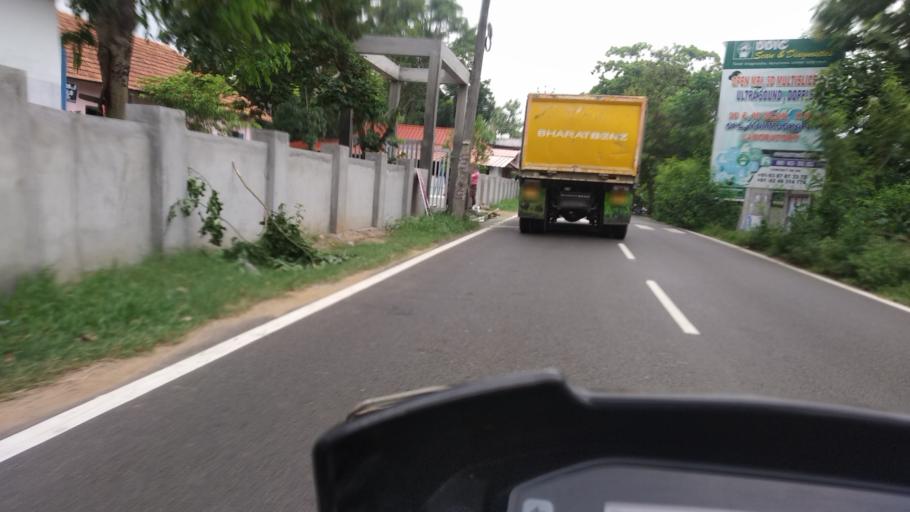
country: IN
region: Kerala
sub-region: Ernakulam
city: Aluva
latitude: 10.1549
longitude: 76.2792
